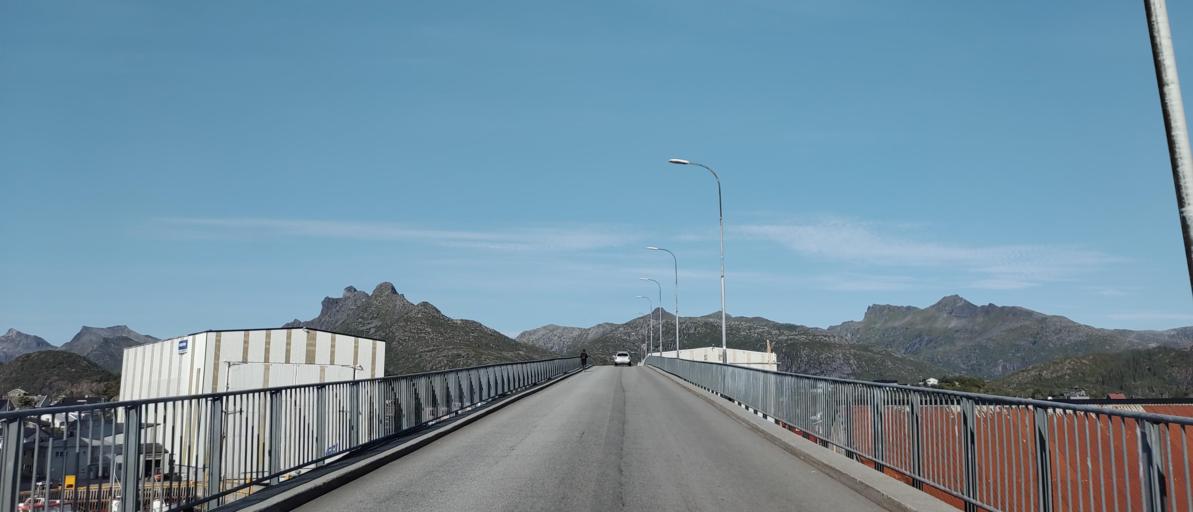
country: NO
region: Nordland
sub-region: Vagan
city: Svolvaer
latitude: 68.2355
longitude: 14.5779
